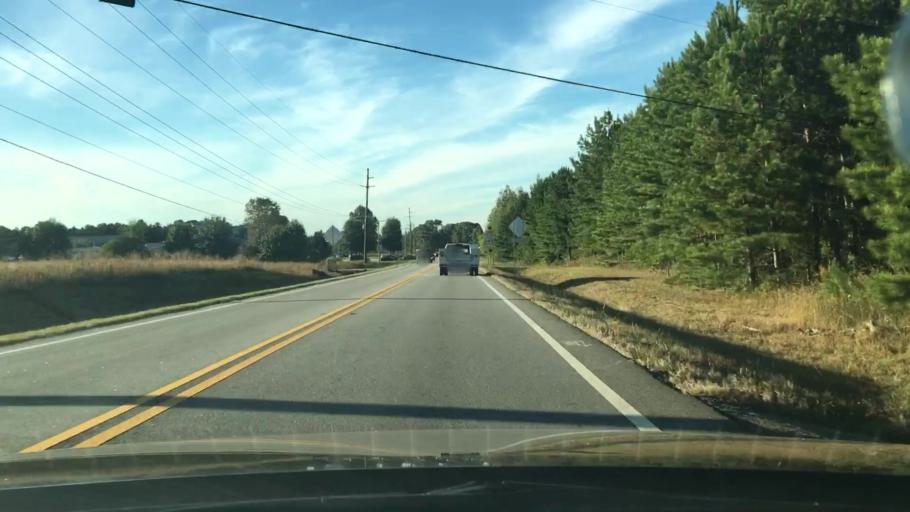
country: US
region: Georgia
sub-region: Coweta County
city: Senoia
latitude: 33.3024
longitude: -84.5953
